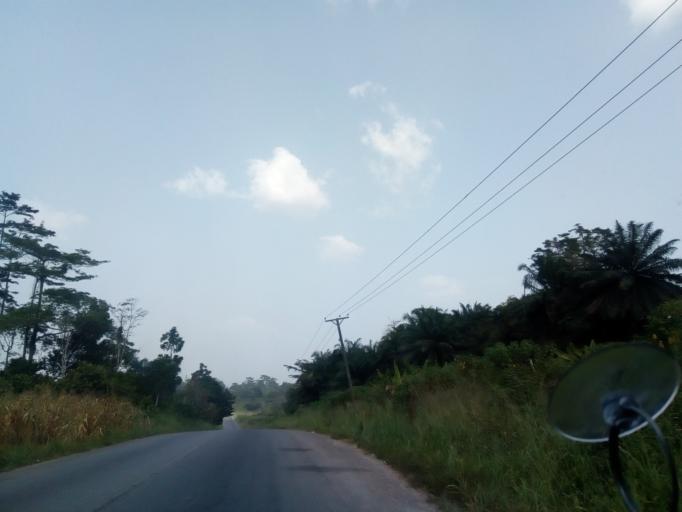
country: GH
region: Eastern
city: Suhum
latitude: 6.0502
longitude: -0.4087
